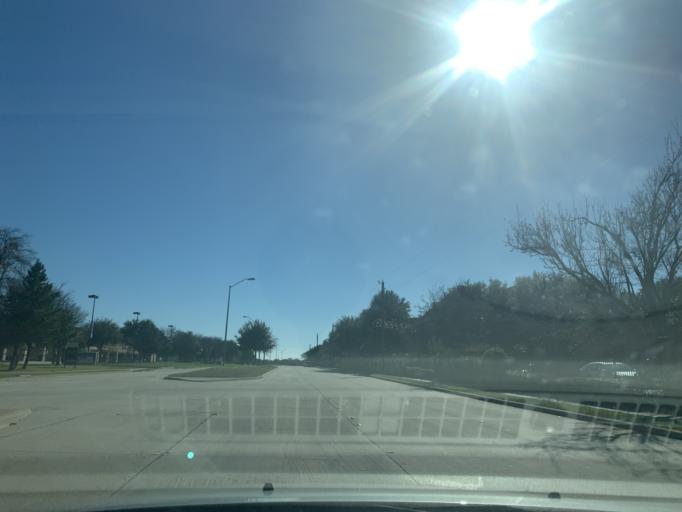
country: US
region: Texas
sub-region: Denton County
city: The Colony
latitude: 33.0494
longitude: -96.8331
